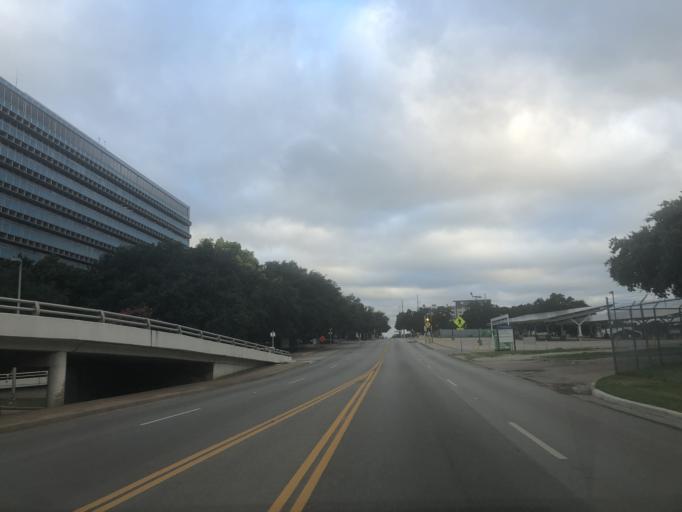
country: US
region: Texas
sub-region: Dallas County
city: University Park
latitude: 32.8231
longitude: -96.8445
